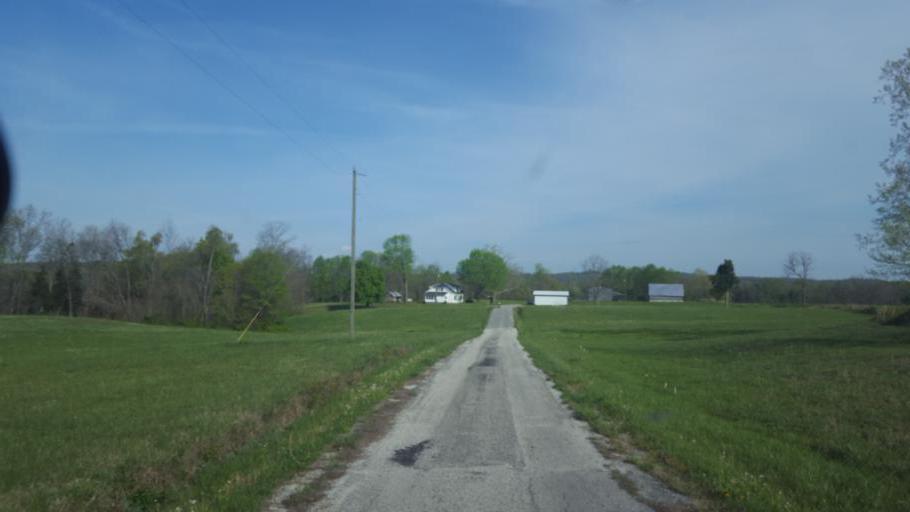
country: US
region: Kentucky
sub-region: Edmonson County
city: Brownsville
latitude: 37.3324
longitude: -86.1133
